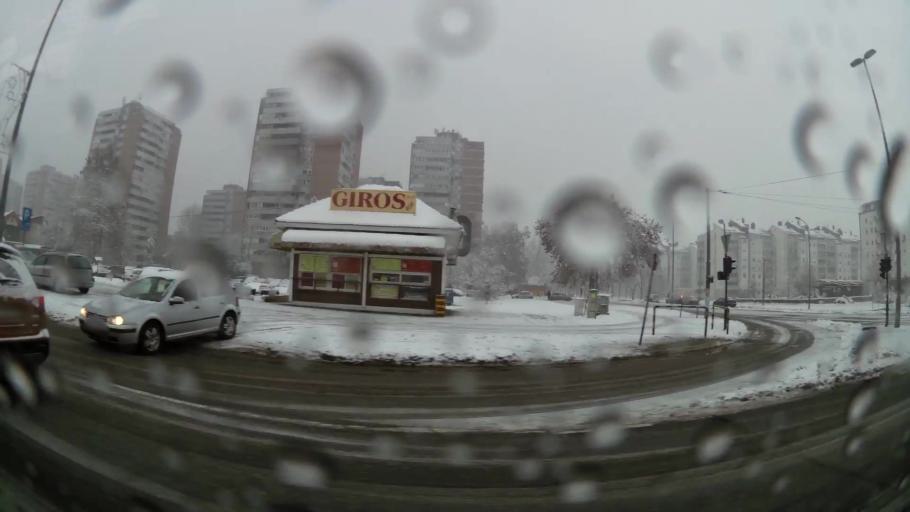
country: RS
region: Central Serbia
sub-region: Belgrade
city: Cukarica
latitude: 44.7978
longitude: 20.3716
